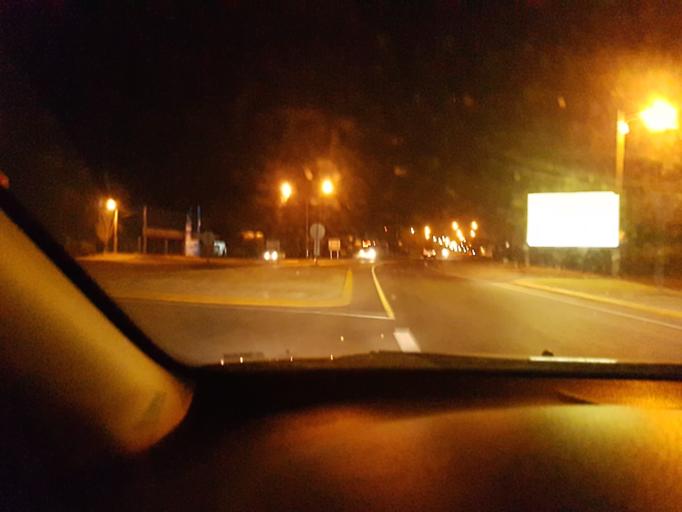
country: AR
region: Cordoba
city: Villa Allende
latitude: -31.3005
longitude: -64.2781
